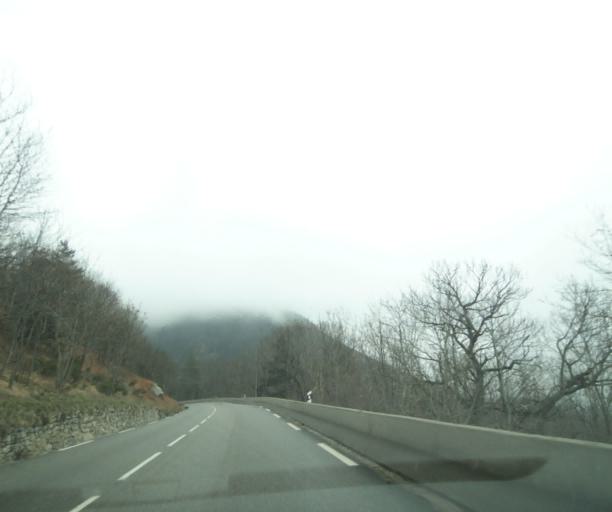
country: FR
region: Rhone-Alpes
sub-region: Departement de l'Ardeche
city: Thueyts
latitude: 44.6884
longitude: 4.0602
